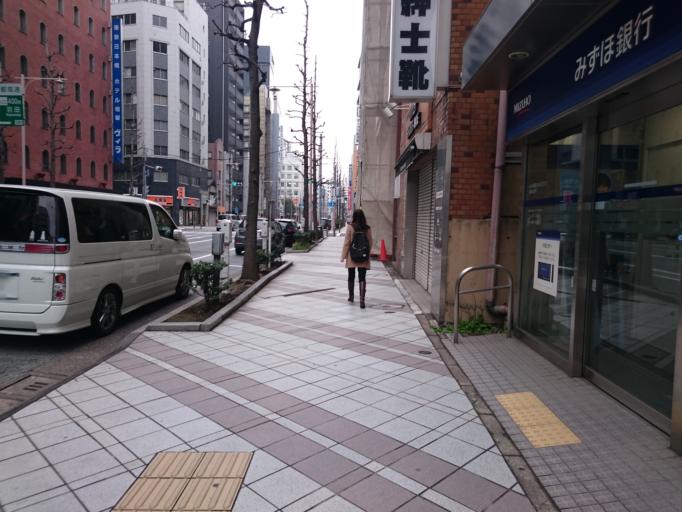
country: JP
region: Tokyo
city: Tokyo
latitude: 35.6887
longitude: 139.7803
